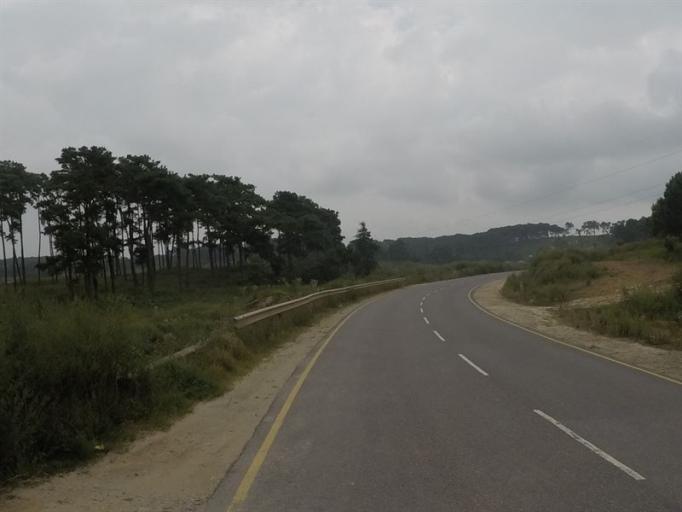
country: IN
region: Meghalaya
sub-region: East Khasi Hills
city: Shillong
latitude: 25.4950
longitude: 92.1733
